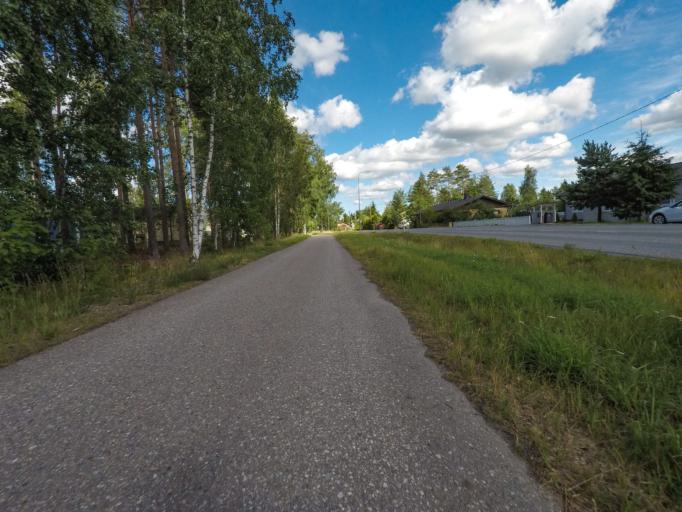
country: FI
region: South Karelia
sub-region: Lappeenranta
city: Lappeenranta
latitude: 61.0786
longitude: 28.3198
